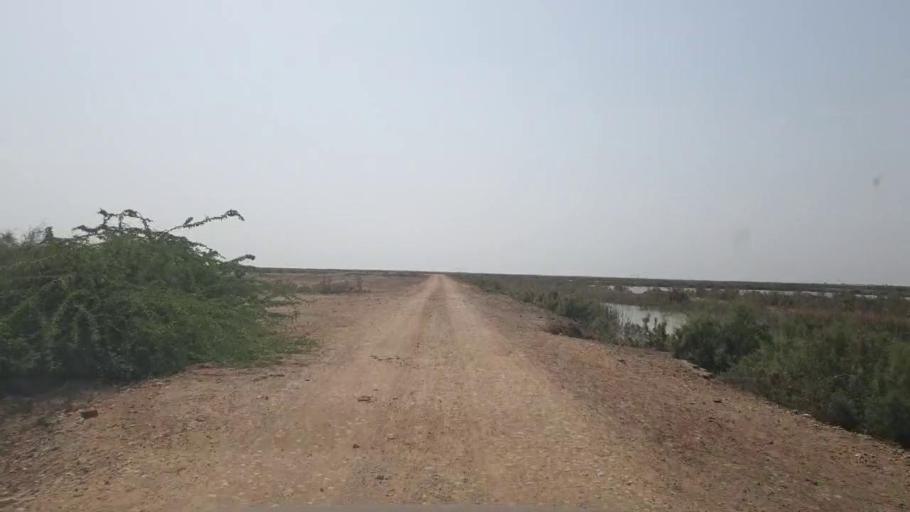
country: PK
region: Sindh
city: Jati
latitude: 24.3759
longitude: 68.6020
